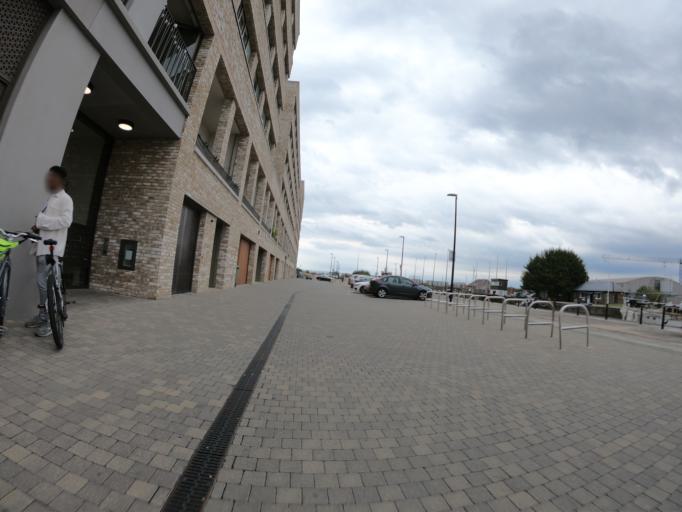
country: GB
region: England
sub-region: Greater London
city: Woolwich
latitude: 51.5054
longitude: 0.0753
